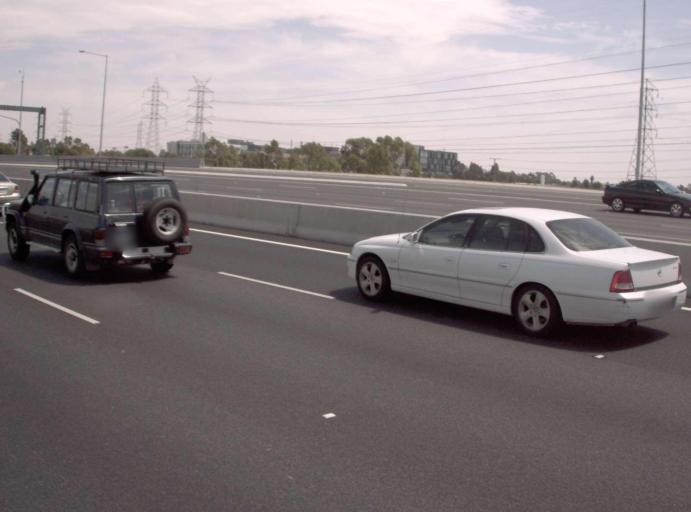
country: AU
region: Victoria
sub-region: Brimbank
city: Sunshine North
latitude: -37.7578
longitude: 144.8230
